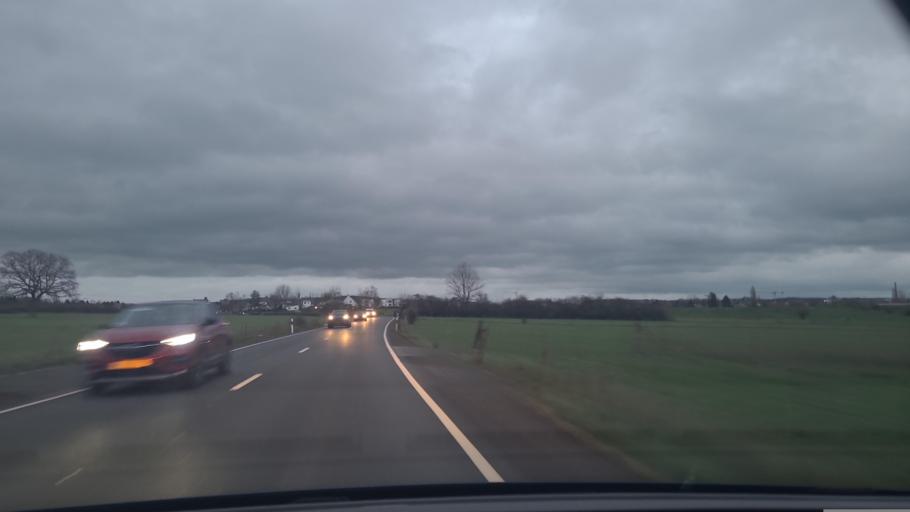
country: LU
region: Luxembourg
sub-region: Canton de Capellen
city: Bascharage
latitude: 49.5684
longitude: 5.8950
